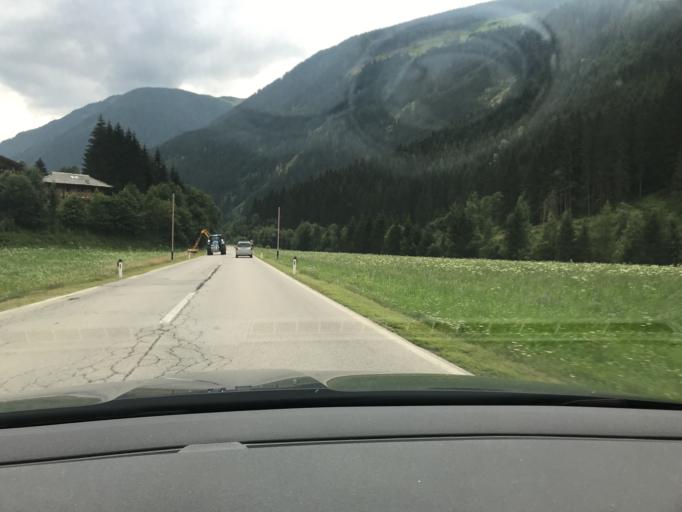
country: AT
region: Tyrol
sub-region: Politischer Bezirk Lienz
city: Hopfgarten in Defereggen
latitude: 46.9212
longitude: 12.4803
